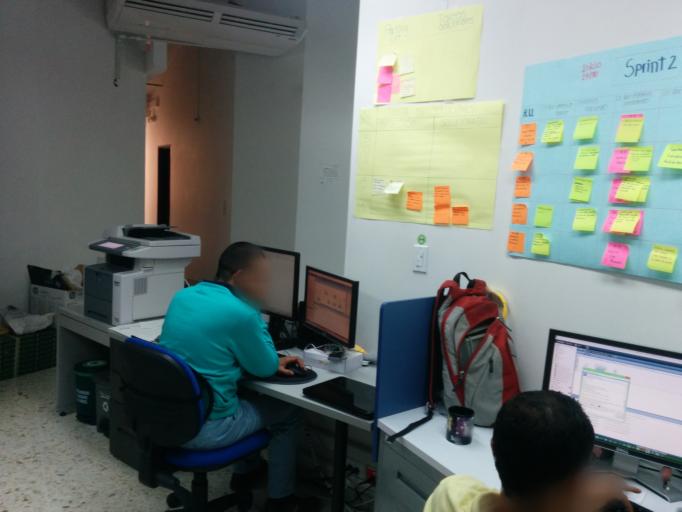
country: CO
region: Valle del Cauca
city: Cali
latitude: 3.4250
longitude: -76.5441
